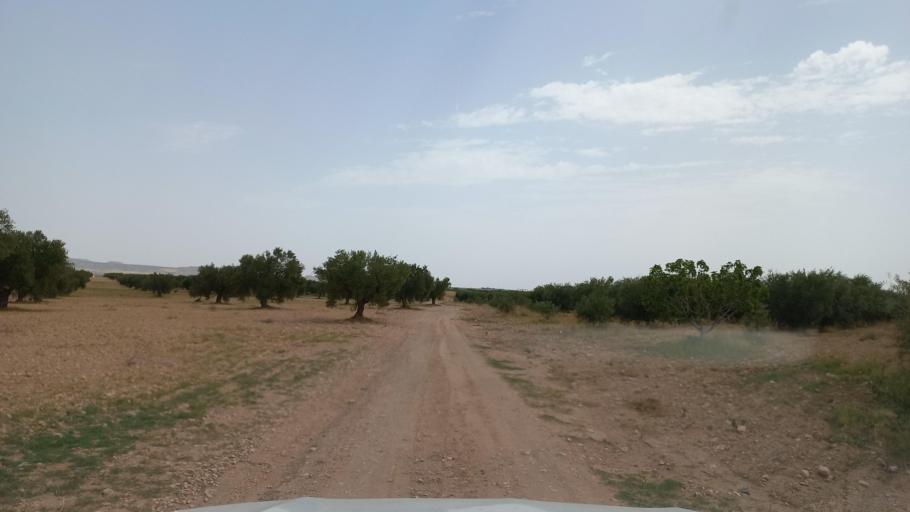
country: TN
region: Al Qasrayn
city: Kasserine
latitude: 35.2894
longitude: 9.0256
